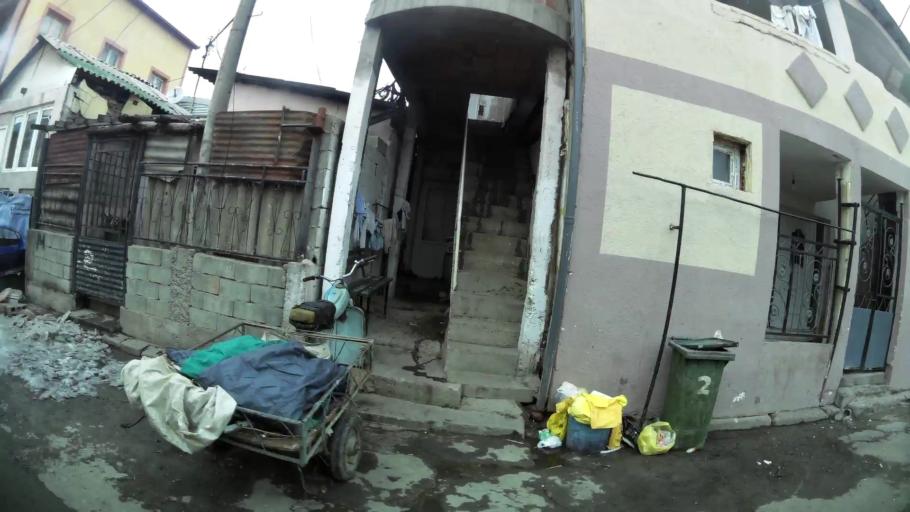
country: MK
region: Suto Orizari
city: Suto Orizare
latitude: 42.0452
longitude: 21.4256
